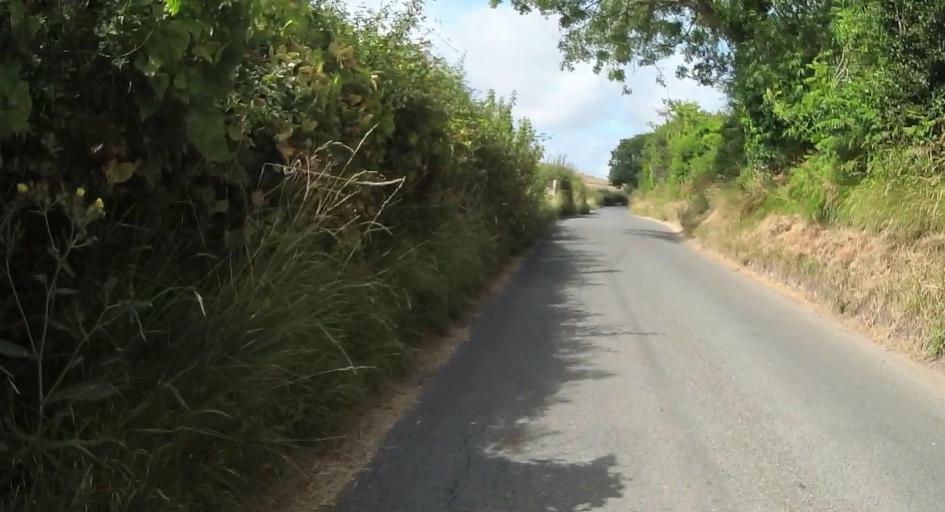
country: GB
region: England
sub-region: Dorset
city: Swanage
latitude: 50.6151
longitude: -1.9806
